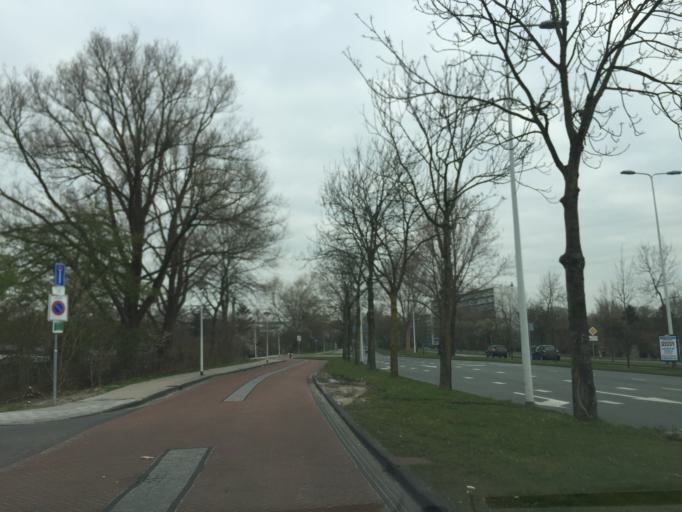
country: NL
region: South Holland
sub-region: Gemeente Leiden
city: Leiden
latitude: 52.1695
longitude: 4.5100
